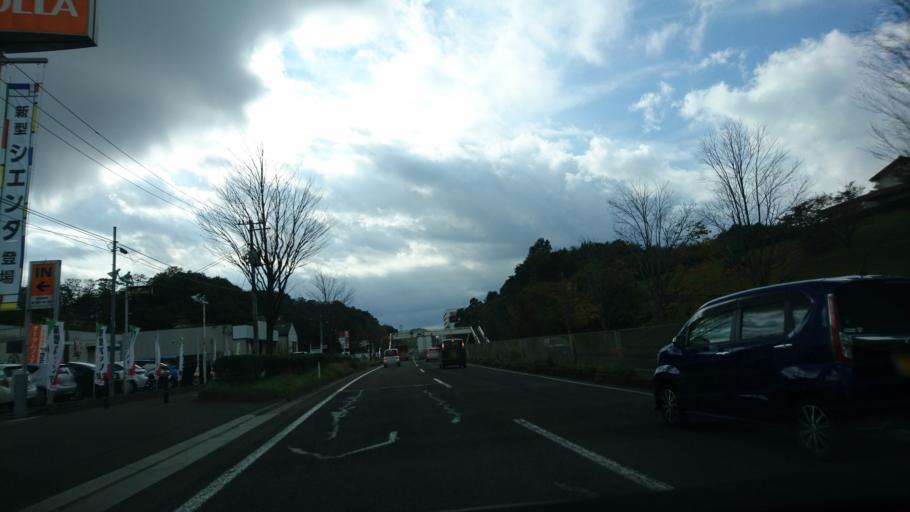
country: JP
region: Miyagi
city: Tomiya
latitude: 38.3749
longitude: 140.8740
